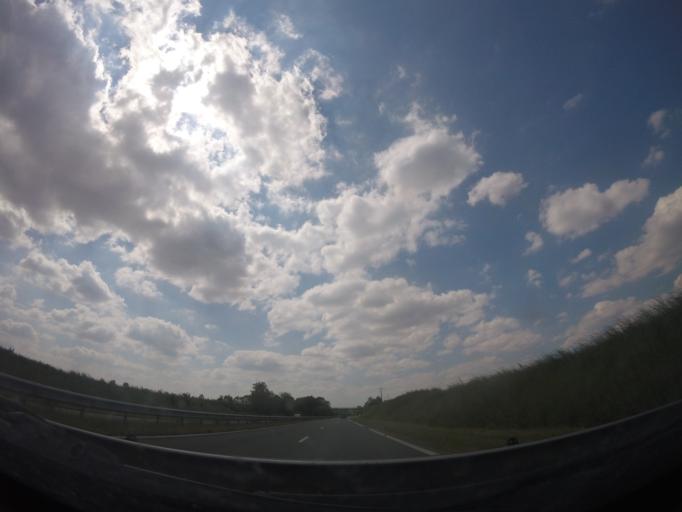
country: FR
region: Poitou-Charentes
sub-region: Departement de la Charente-Maritime
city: Saint-Porchaire
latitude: 45.8131
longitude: -0.7779
